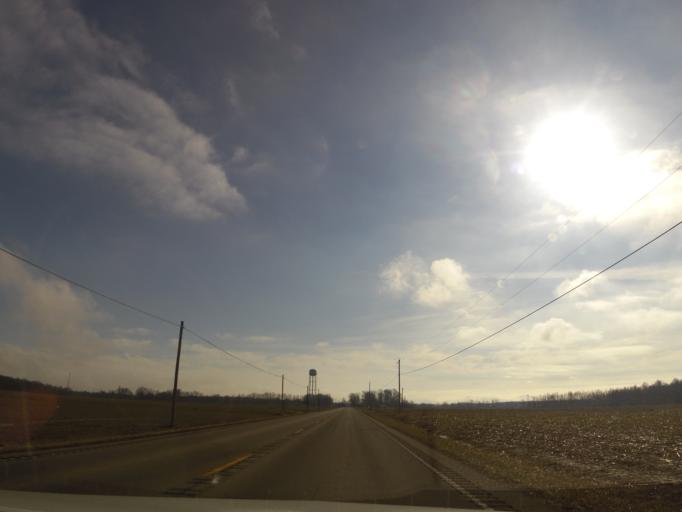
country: US
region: Indiana
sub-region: Jennings County
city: North Vernon
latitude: 38.8987
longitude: -85.5331
